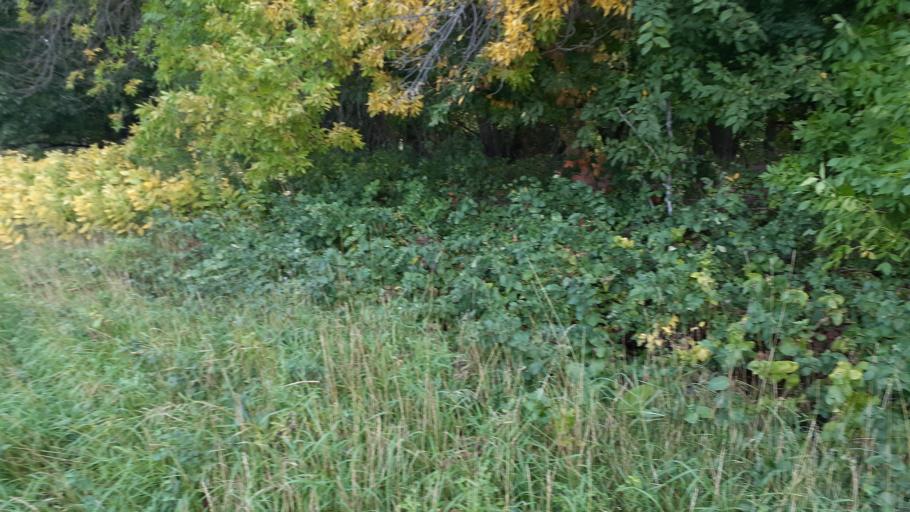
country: US
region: Minnesota
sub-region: Clay County
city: Oakport
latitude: 46.9094
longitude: -96.7646
